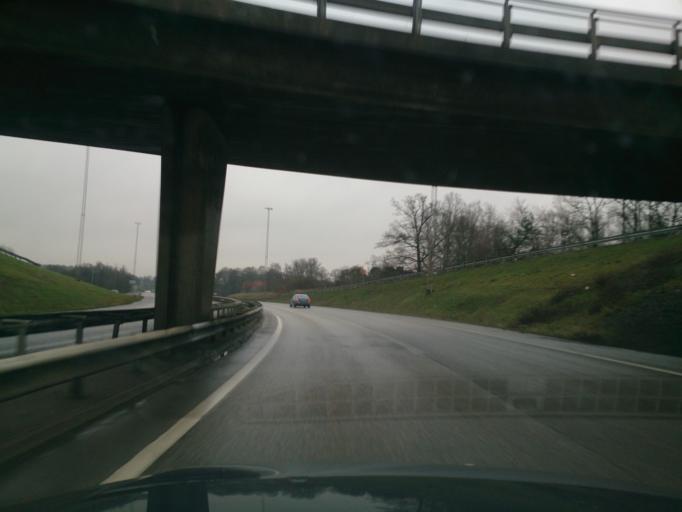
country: SE
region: OEstergoetland
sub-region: Norrkopings Kommun
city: Norrkoping
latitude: 58.5846
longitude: 16.1495
